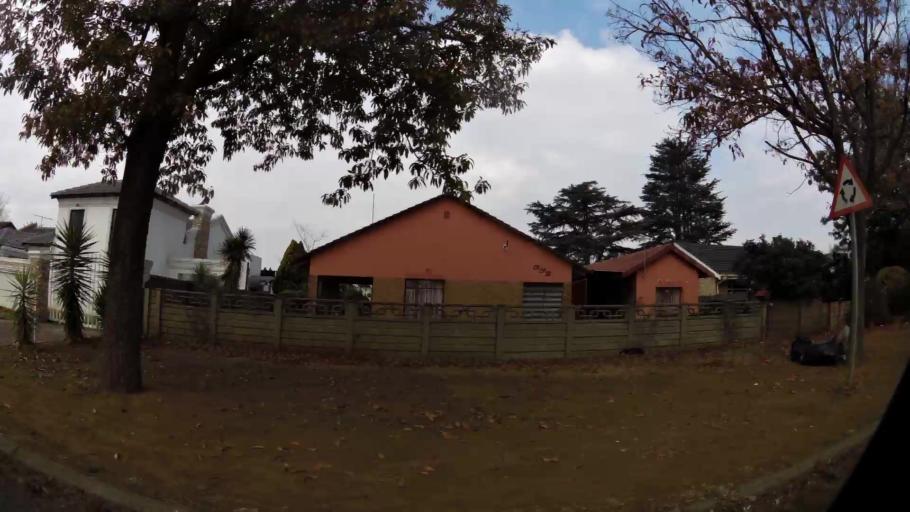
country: ZA
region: Gauteng
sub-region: Sedibeng District Municipality
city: Vanderbijlpark
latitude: -26.6963
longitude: 27.8495
